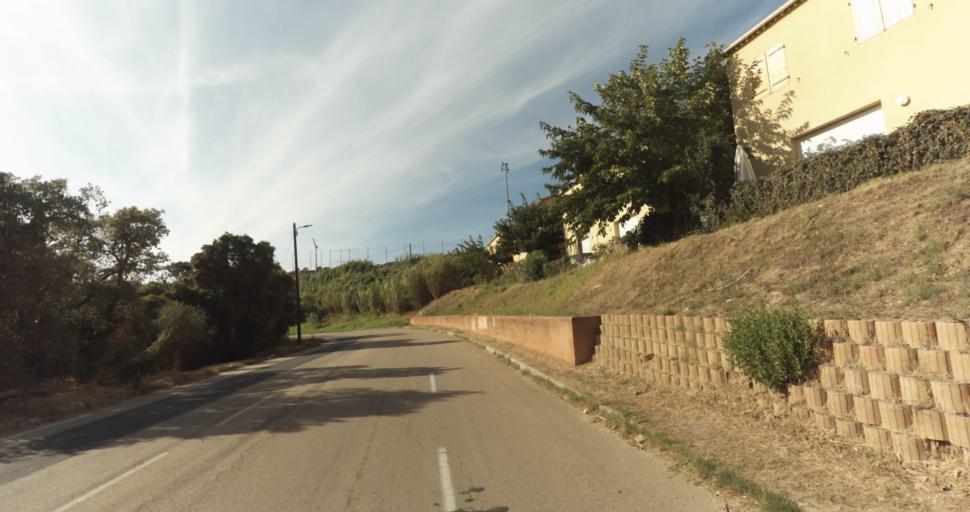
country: FR
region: Corsica
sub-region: Departement de la Corse-du-Sud
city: Ajaccio
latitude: 41.9302
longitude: 8.7802
